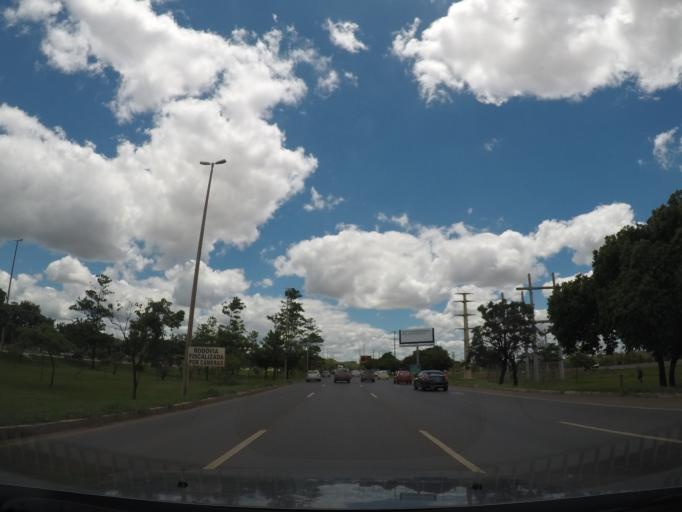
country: BR
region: Federal District
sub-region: Brasilia
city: Brasilia
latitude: -15.7810
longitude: -47.9400
